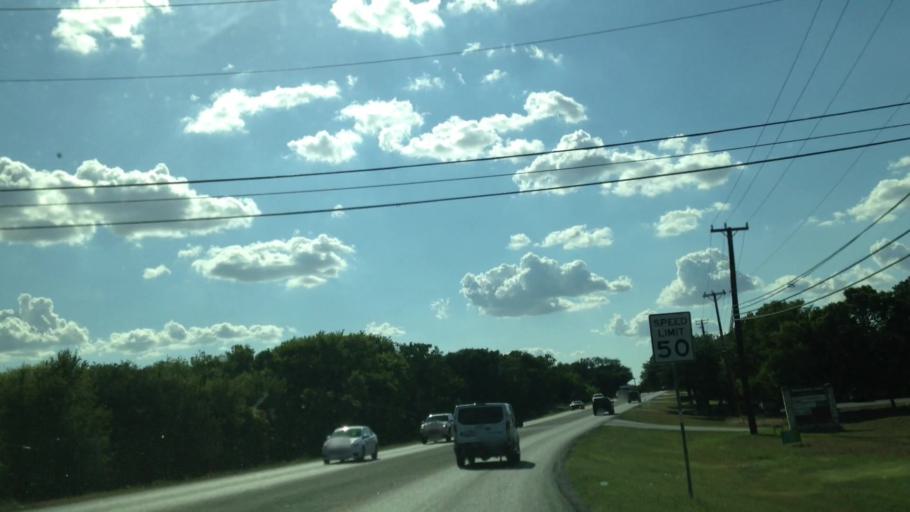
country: US
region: Texas
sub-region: Comal County
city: Garden Ridge
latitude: 29.6209
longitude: -98.2962
